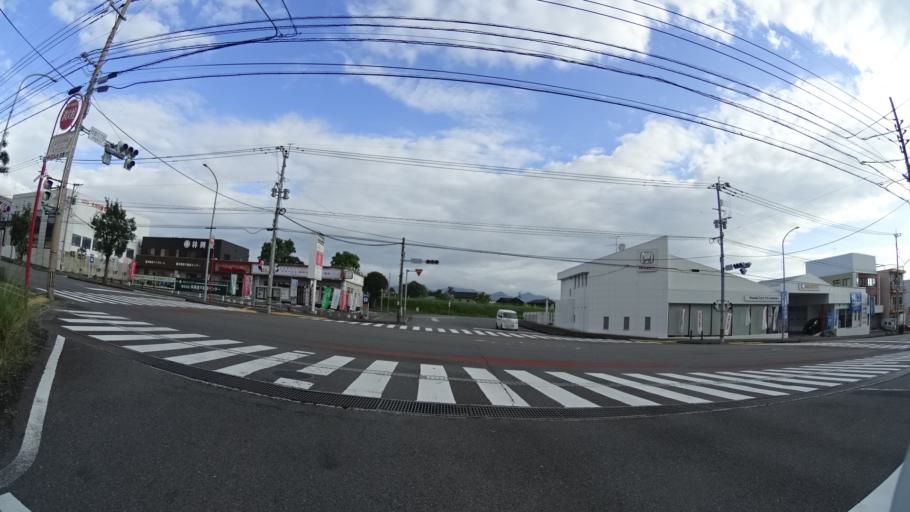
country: JP
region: Oita
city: Beppu
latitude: 33.3052
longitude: 131.4946
